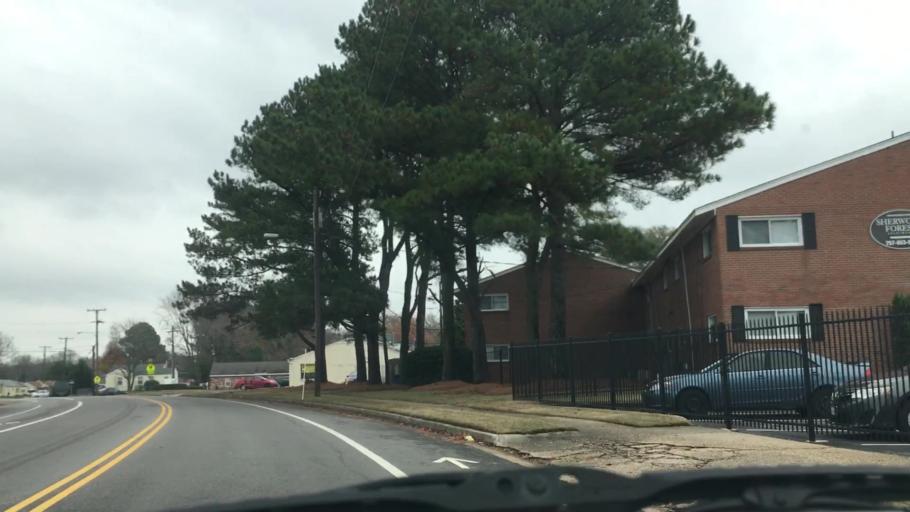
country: US
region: Virginia
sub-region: City of Norfolk
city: Norfolk
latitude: 36.8759
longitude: -76.2385
